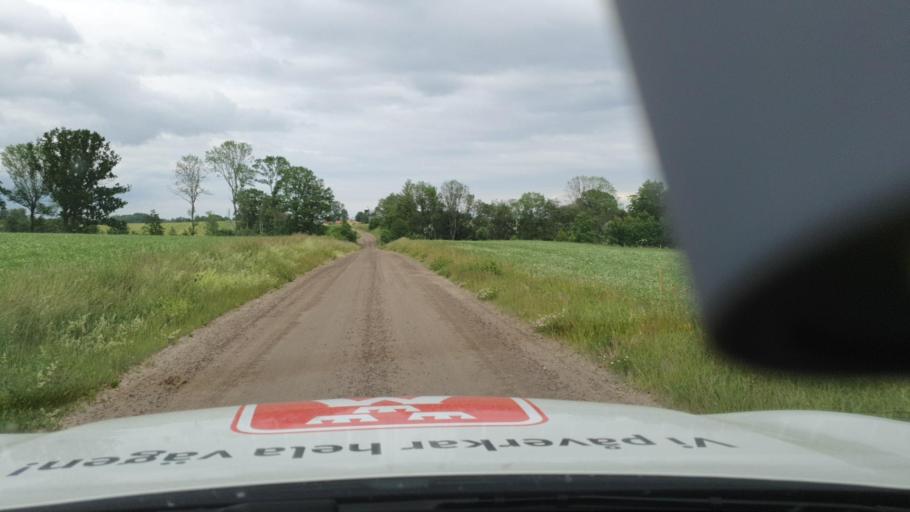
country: SE
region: Vaestra Goetaland
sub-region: Hjo Kommun
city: Hjo
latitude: 58.2081
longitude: 14.1803
